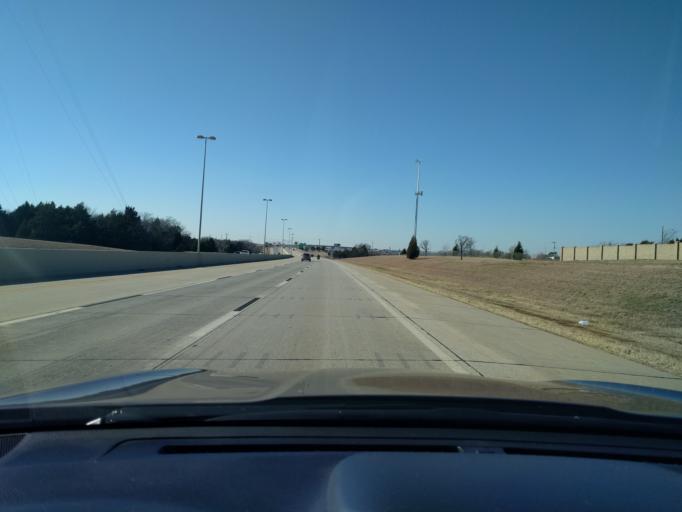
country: US
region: Oklahoma
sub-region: Oklahoma County
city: Edmond
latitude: 35.6011
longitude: -97.4865
